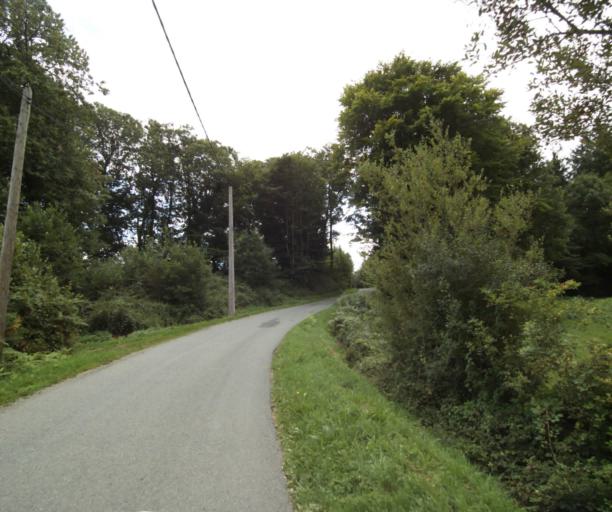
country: FR
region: Limousin
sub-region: Departement de la Correze
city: Sainte-Fortunade
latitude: 45.1998
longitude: 1.8088
